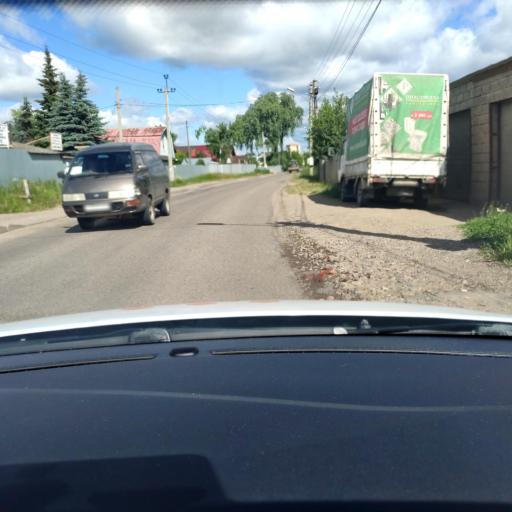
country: RU
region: Tatarstan
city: Vysokaya Gora
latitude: 55.8593
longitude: 49.2412
